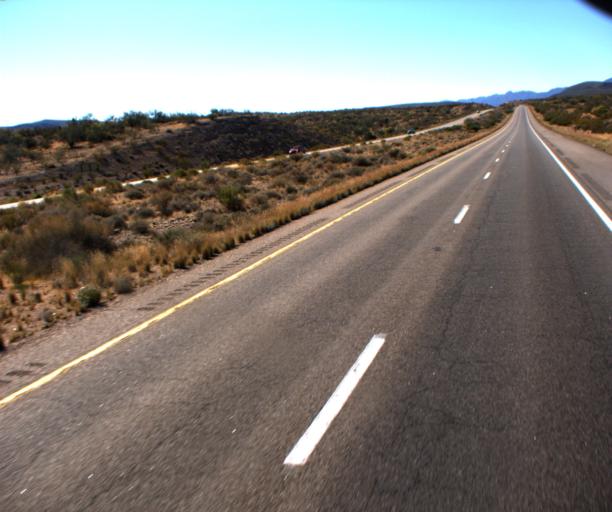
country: US
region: Arizona
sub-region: Yavapai County
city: Bagdad
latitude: 34.6077
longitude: -113.5234
